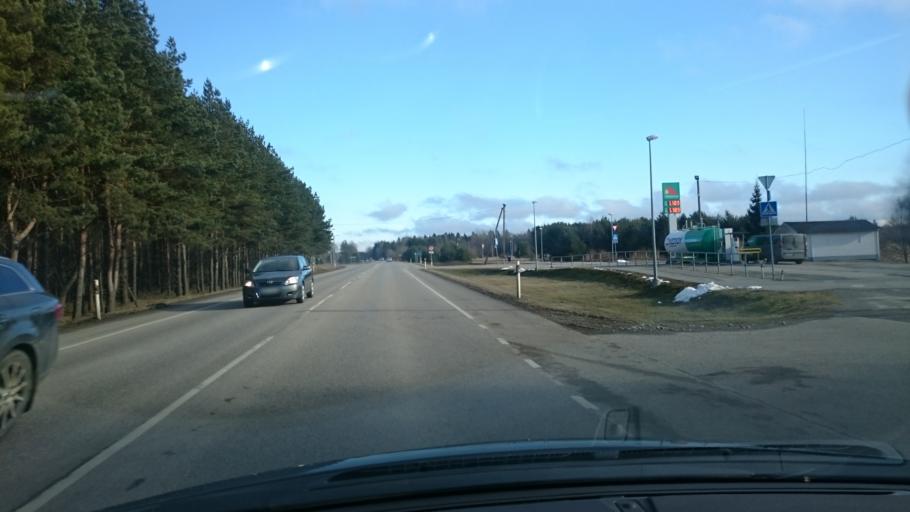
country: EE
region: Harju
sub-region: Harku vald
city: Tabasalu
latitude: 59.4345
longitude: 24.5870
